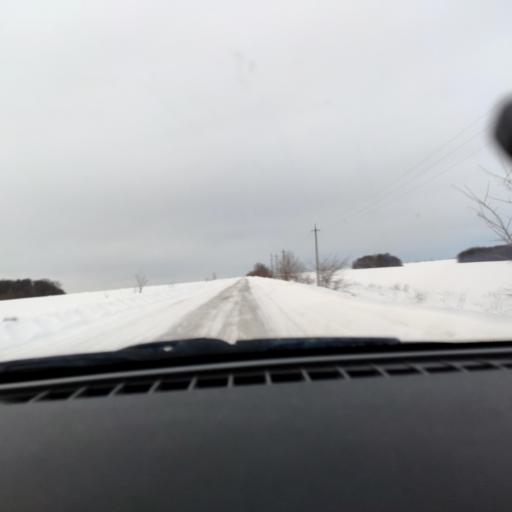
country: RU
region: Bashkortostan
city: Iglino
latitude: 54.7443
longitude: 56.5341
